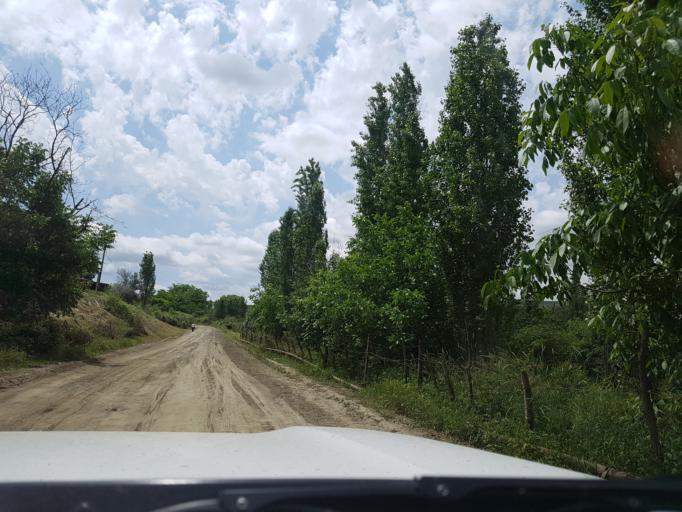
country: TM
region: Ahal
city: Baharly
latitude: 38.1966
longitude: 57.0044
